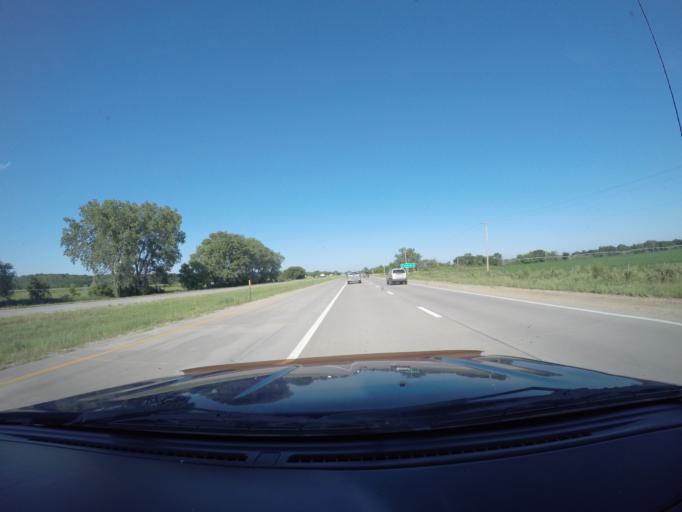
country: US
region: Kansas
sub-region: Shawnee County
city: Topeka
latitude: 39.0872
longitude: -95.5405
